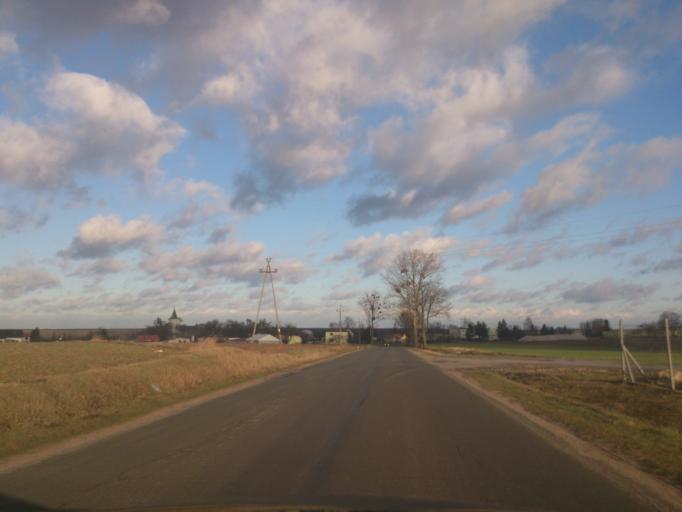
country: PL
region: Kujawsko-Pomorskie
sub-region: Powiat golubsko-dobrzynski
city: Ciechocin
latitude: 53.0537
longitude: 18.9180
